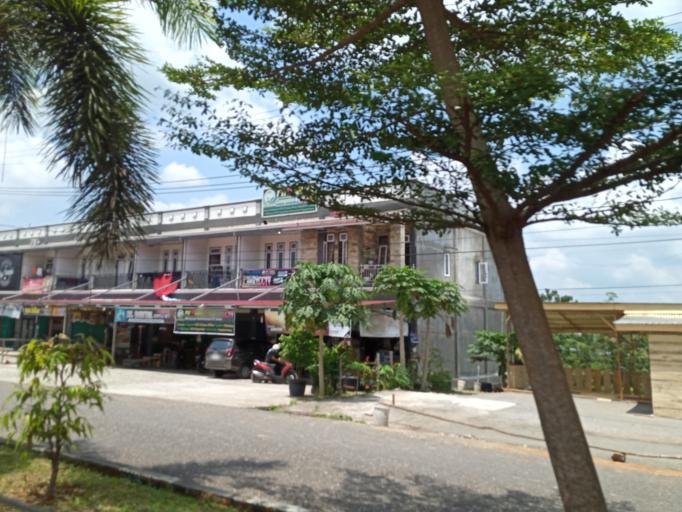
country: ID
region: Jambi
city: Bangko
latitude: -2.0584
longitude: 102.2776
